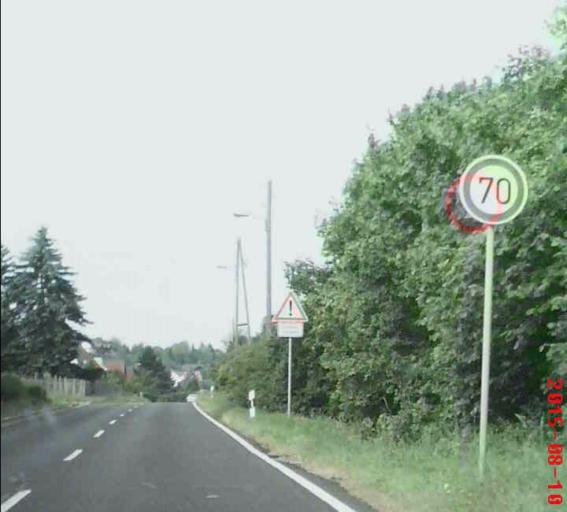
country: DE
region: Thuringia
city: Dillstadt
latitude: 50.5761
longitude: 10.5259
